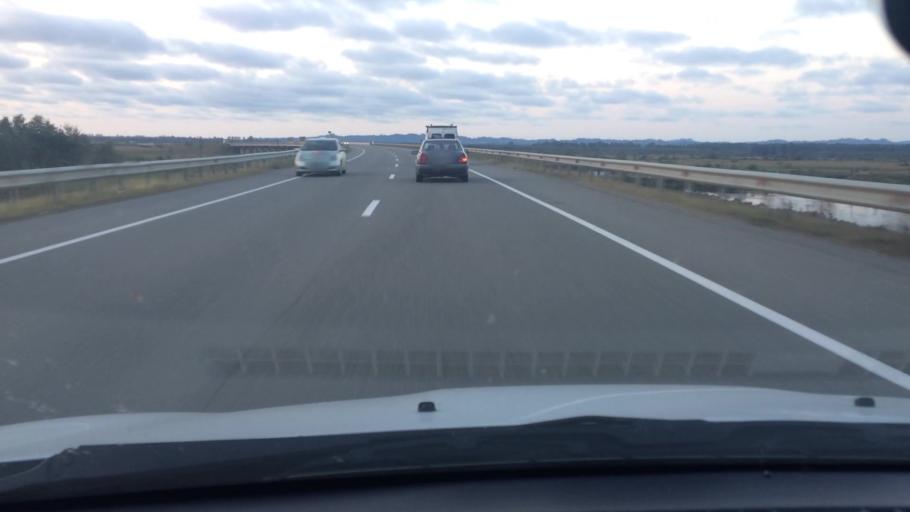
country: GE
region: Ajaria
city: Ochkhamuri
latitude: 41.8628
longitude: 41.8377
